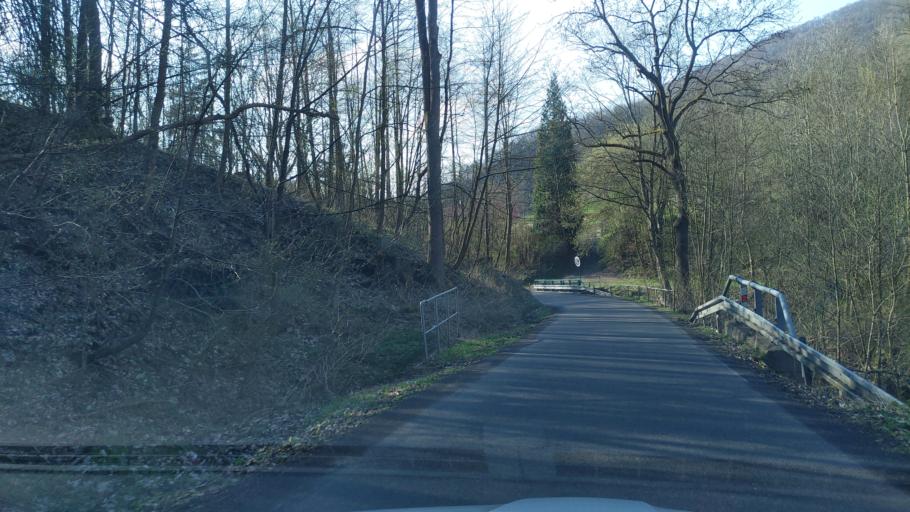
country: CZ
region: Ustecky
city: Povrly
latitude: 50.7036
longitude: 14.2311
